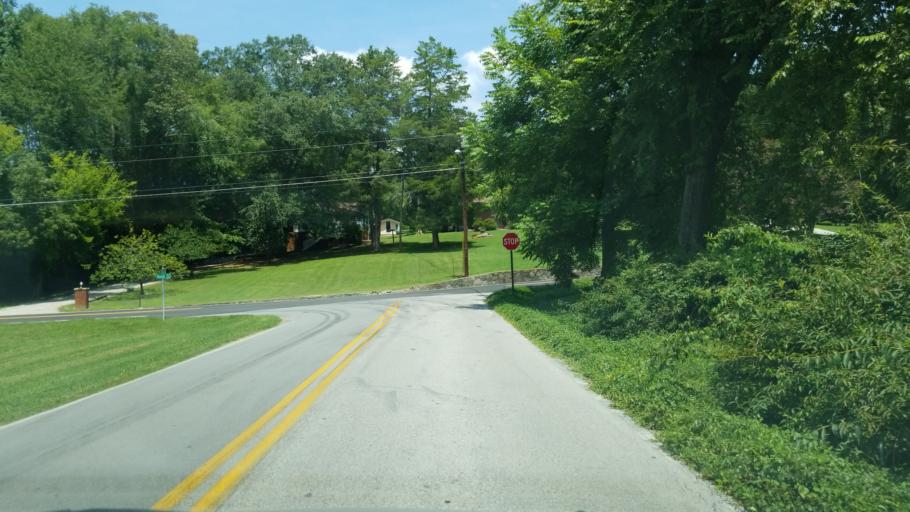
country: US
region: Tennessee
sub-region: Hamilton County
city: Middle Valley
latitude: 35.1288
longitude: -85.2117
